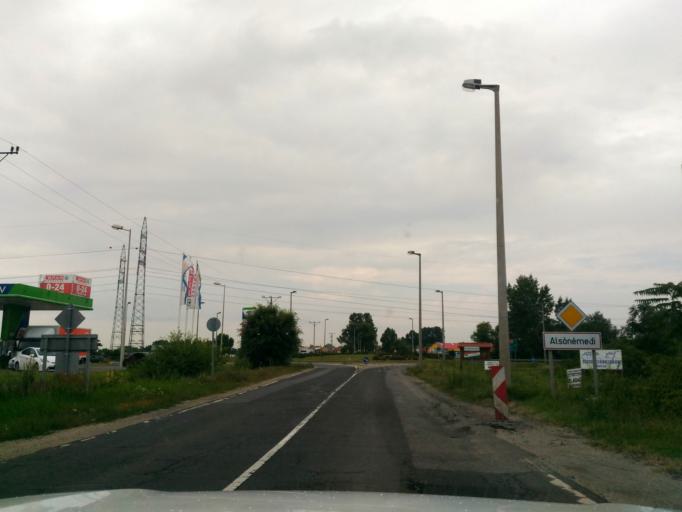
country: HU
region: Pest
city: Alsonemedi
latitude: 47.3018
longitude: 19.1805
